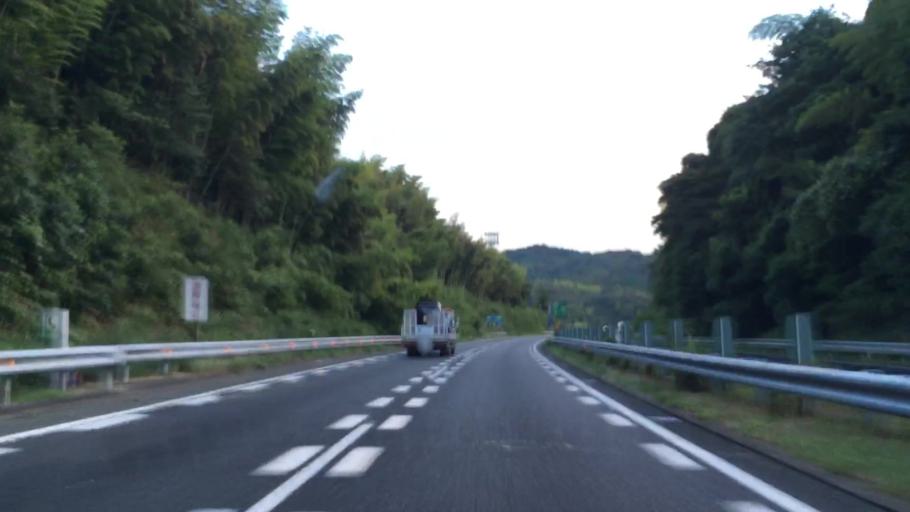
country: JP
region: Yamaguchi
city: Shimonoseki
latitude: 33.9339
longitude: 130.9961
